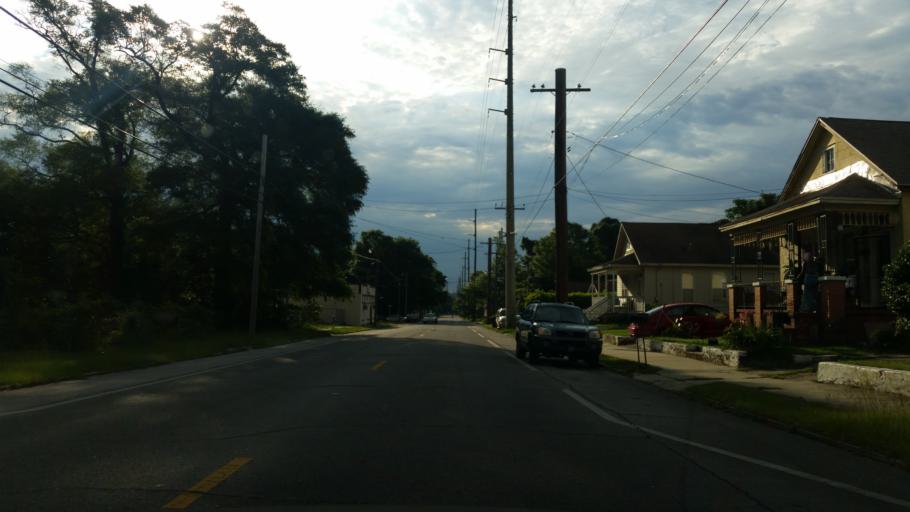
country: US
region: Florida
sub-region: Escambia County
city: Pensacola
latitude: 30.4183
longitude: -87.2336
